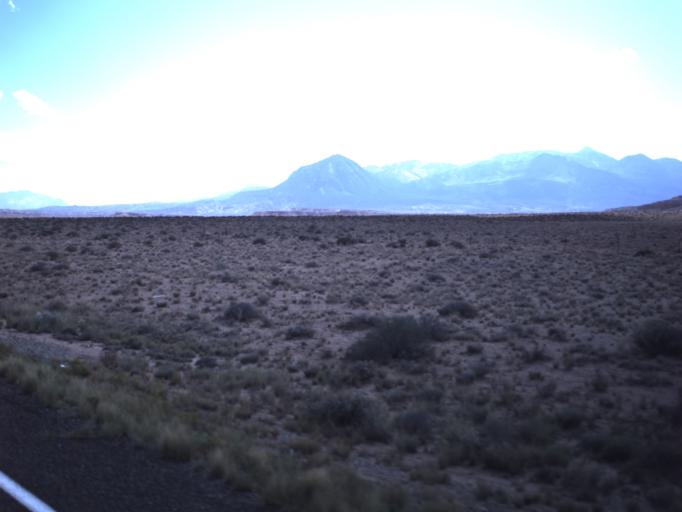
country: US
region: Utah
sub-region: Emery County
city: Ferron
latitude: 38.2742
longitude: -110.6604
